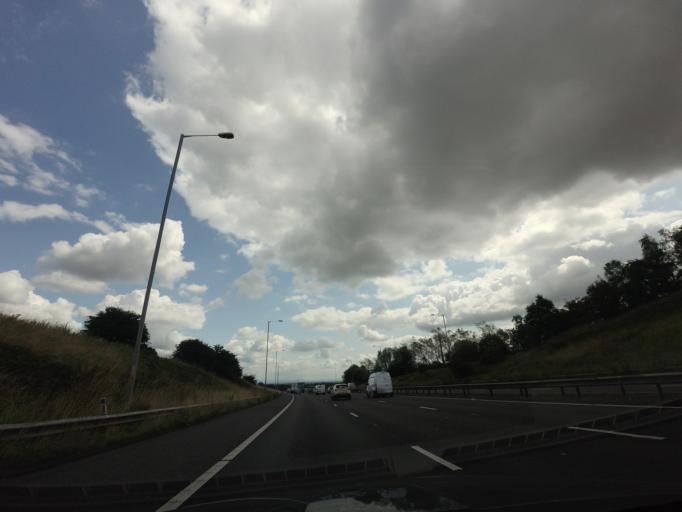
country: GB
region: England
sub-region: St. Helens
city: Billinge
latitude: 53.5123
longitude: -2.6842
